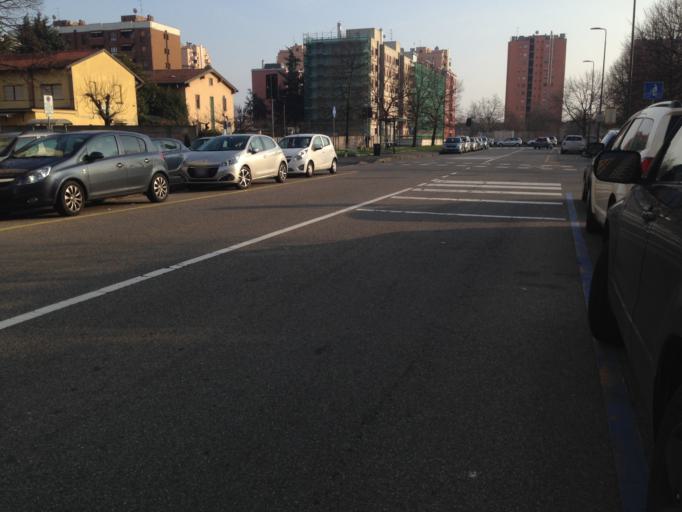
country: IT
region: Lombardy
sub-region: Citta metropolitana di Milano
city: Cesano Boscone
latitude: 45.4723
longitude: 9.1066
